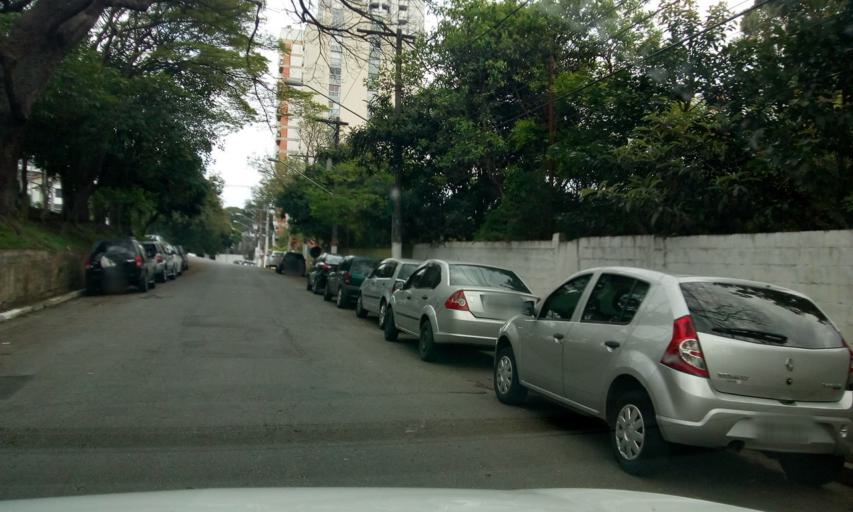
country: BR
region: Sao Paulo
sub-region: Diadema
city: Diadema
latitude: -23.6249
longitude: -46.6641
